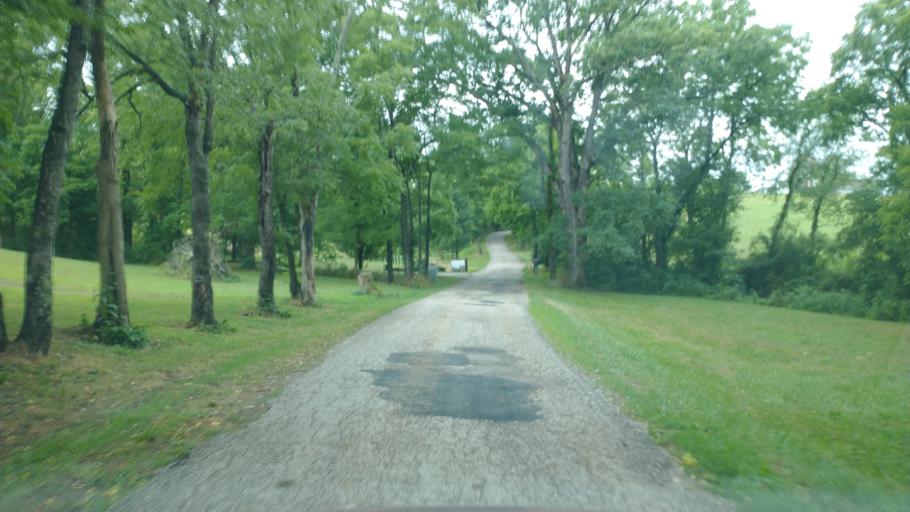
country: US
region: West Virginia
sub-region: Mason County
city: New Haven
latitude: 38.9258
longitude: -81.9666
